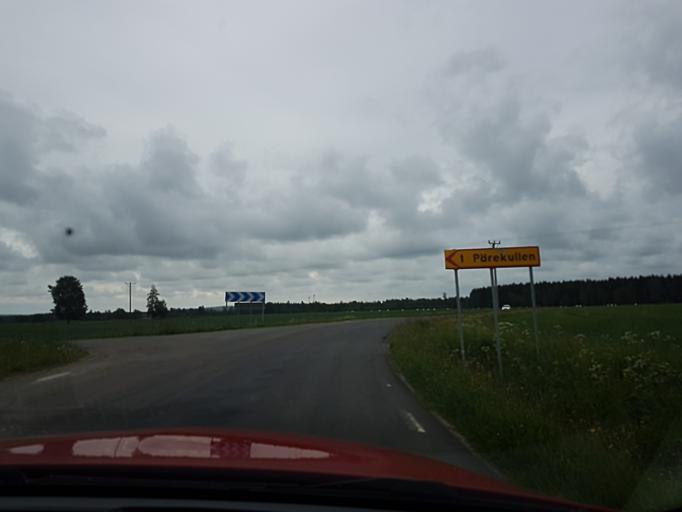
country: SE
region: Vaestra Goetaland
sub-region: Tidaholms Kommun
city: Olofstorp
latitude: 58.3148
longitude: 14.0173
